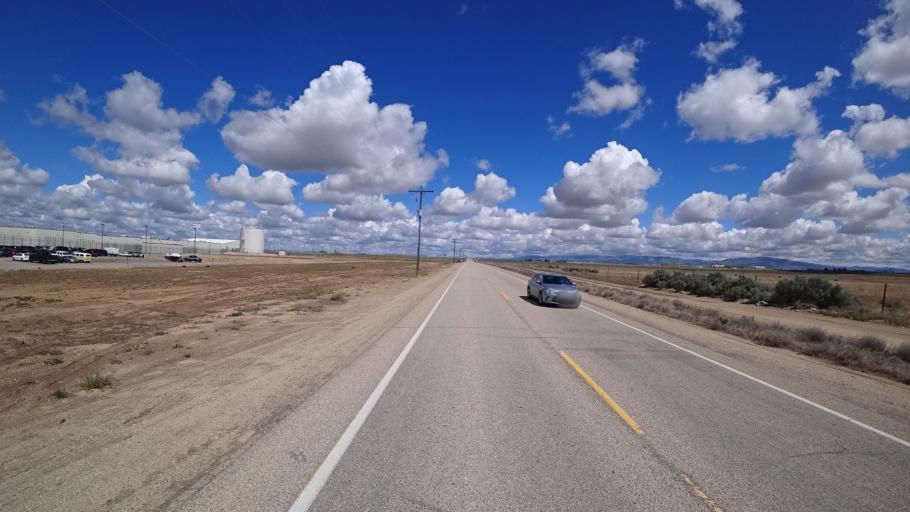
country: US
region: Idaho
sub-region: Ada County
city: Boise
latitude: 43.4699
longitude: -116.2343
